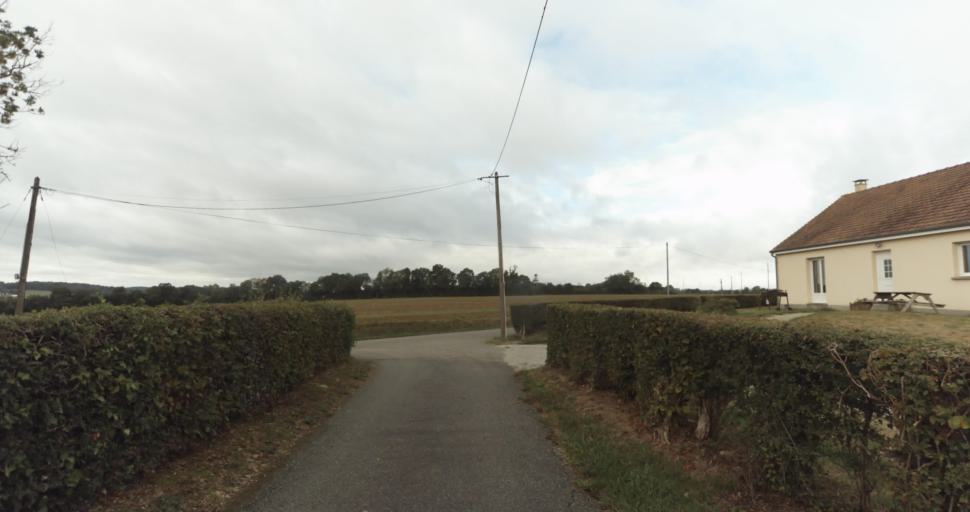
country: FR
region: Lower Normandy
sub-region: Departement de l'Orne
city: Sainte-Gauburge-Sainte-Colombe
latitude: 48.7269
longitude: 0.4408
